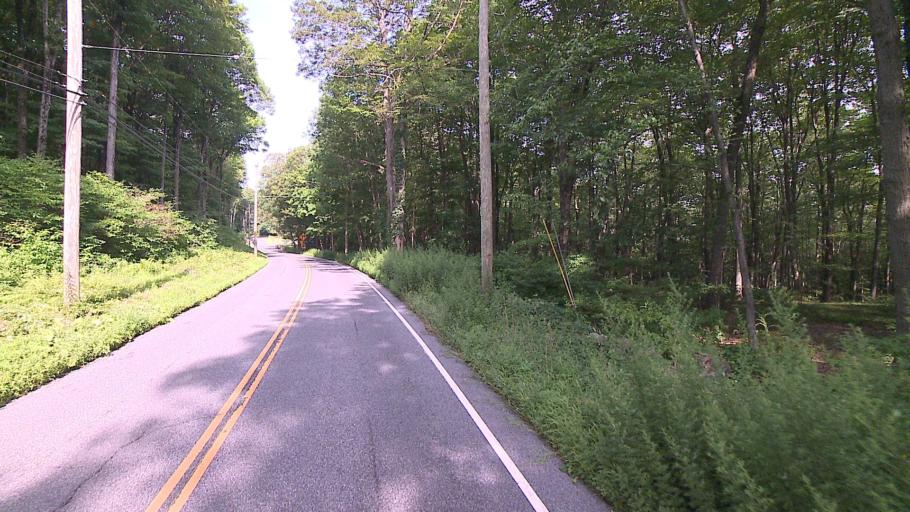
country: US
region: Connecticut
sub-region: Fairfield County
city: Sherman
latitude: 41.5498
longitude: -73.5015
